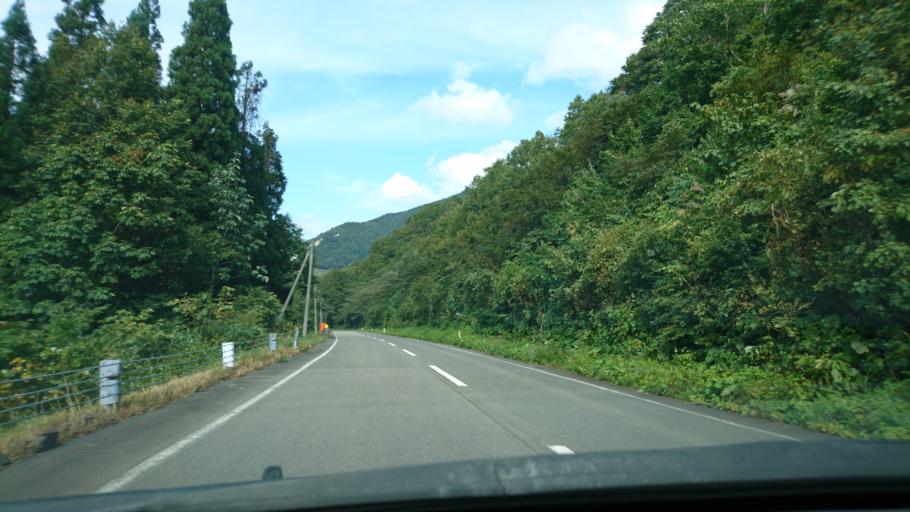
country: JP
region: Akita
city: Yuzawa
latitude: 39.0243
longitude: 140.7284
